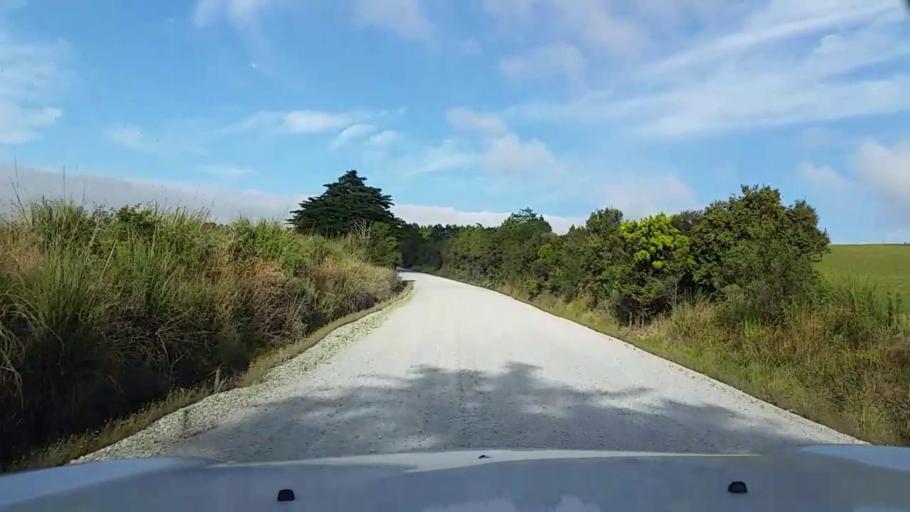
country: NZ
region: Northland
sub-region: Whangarei
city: Maungatapere
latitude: -35.6841
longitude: 174.1882
